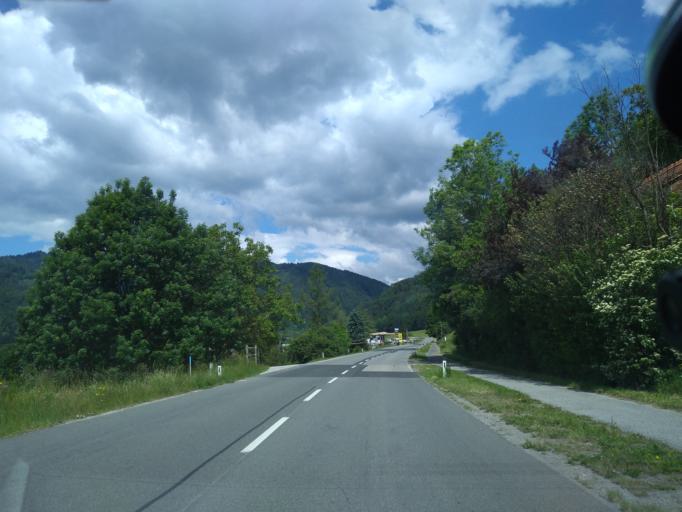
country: AT
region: Styria
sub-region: Politischer Bezirk Graz-Umgebung
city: Frohnleiten
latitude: 47.2408
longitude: 15.3250
